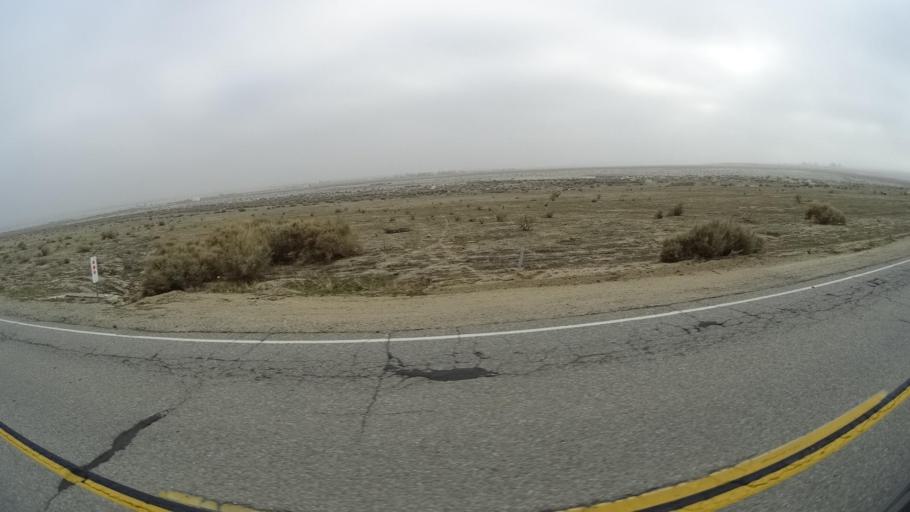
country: US
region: California
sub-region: Kern County
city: South Taft
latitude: 35.1301
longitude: -119.3837
